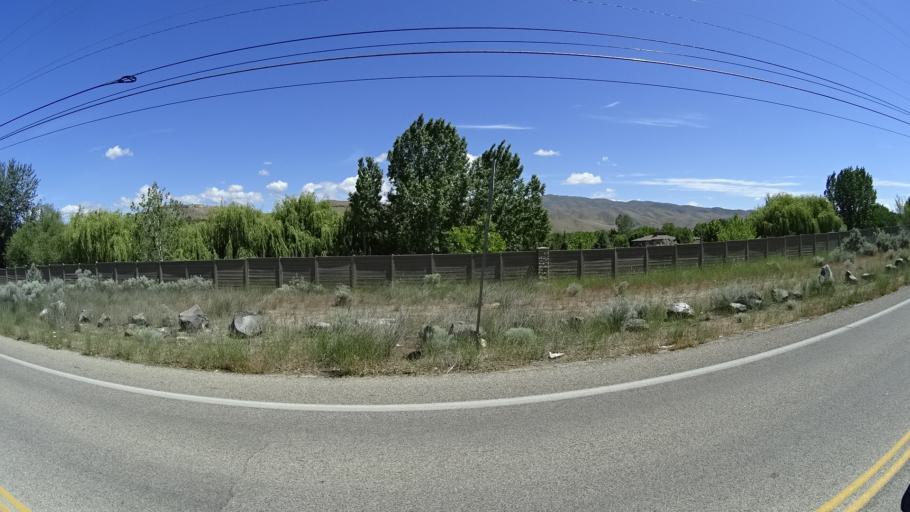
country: US
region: Idaho
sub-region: Ada County
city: Boise
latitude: 43.5718
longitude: -116.1536
